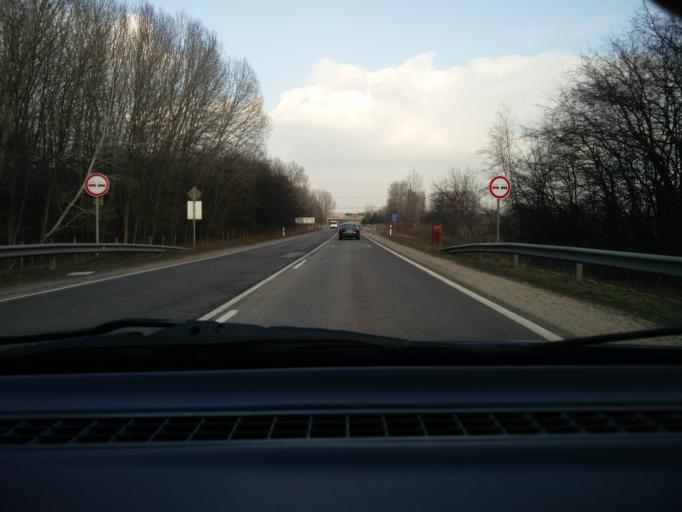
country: HU
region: Pest
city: Albertirsa
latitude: 47.2588
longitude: 19.5781
